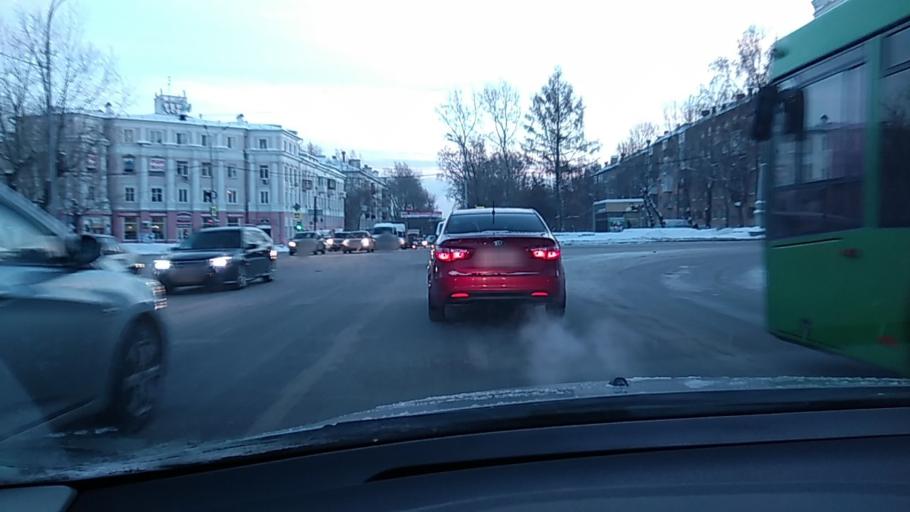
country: RU
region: Sverdlovsk
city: Yekaterinburg
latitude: 56.8265
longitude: 60.6377
